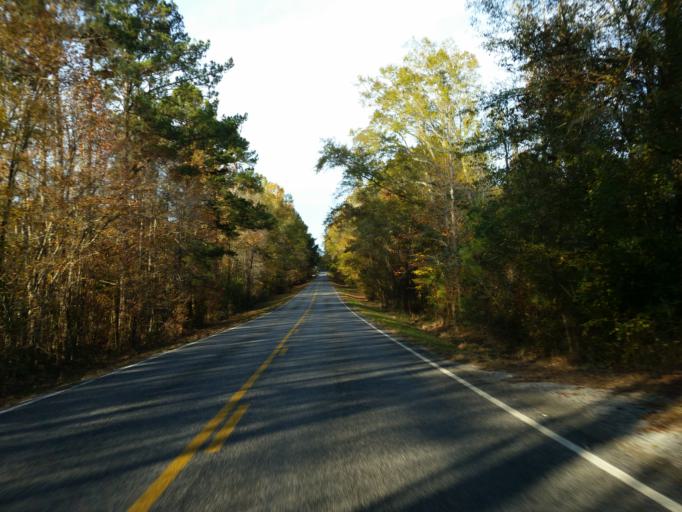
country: US
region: Mississippi
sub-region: Clarke County
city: Quitman
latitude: 31.9703
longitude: -88.9086
